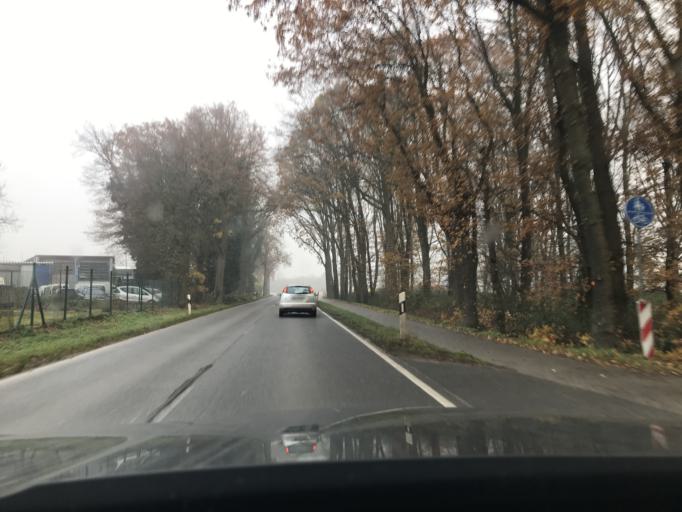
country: DE
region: North Rhine-Westphalia
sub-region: Regierungsbezirk Dusseldorf
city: Nettetal
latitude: 51.2907
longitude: 6.2598
